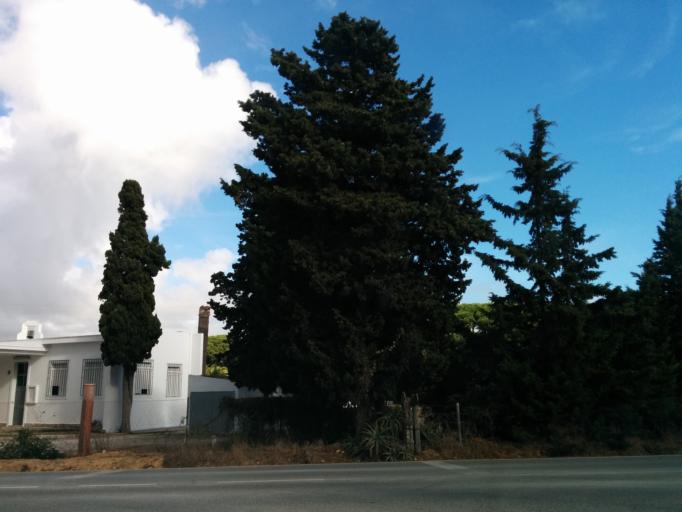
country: ES
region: Andalusia
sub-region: Provincia de Cadiz
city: Vejer de la Frontera
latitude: 36.2017
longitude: -6.0357
